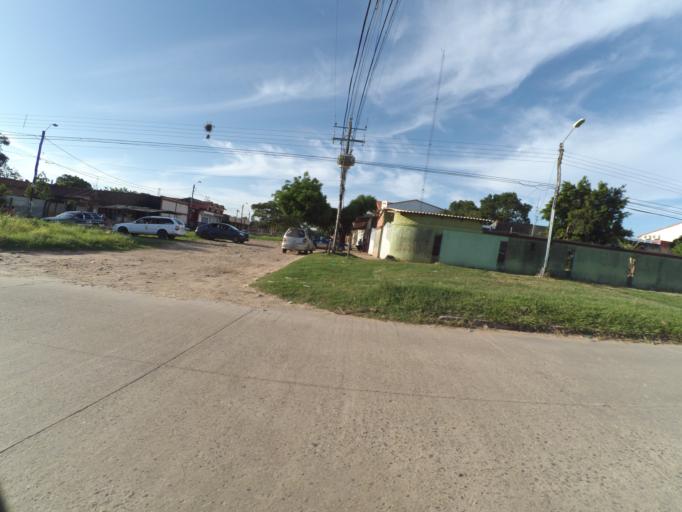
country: BO
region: Santa Cruz
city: Santa Cruz de la Sierra
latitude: -17.7777
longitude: -63.1341
